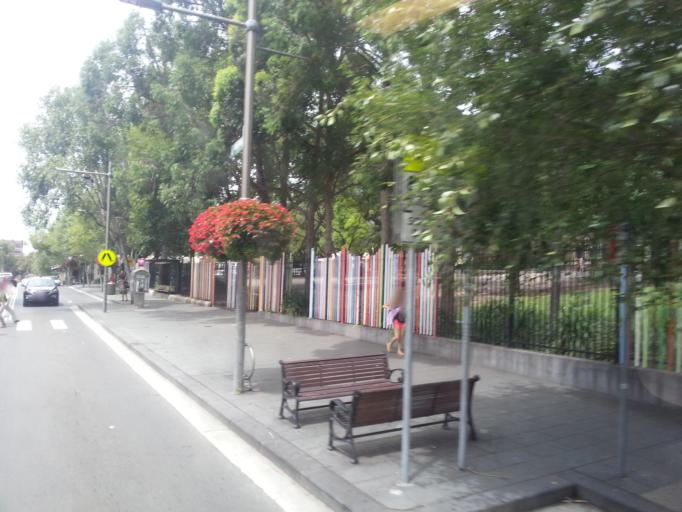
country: AU
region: New South Wales
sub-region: City of Sydney
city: Chippendale
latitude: -33.8831
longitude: 151.1911
